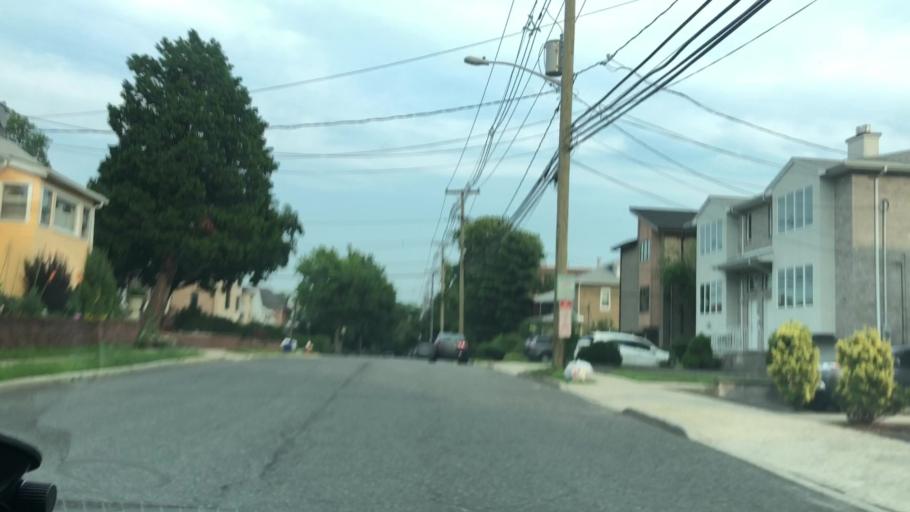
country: US
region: New Jersey
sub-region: Bergen County
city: Fort Lee
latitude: 40.8623
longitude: -73.9614
